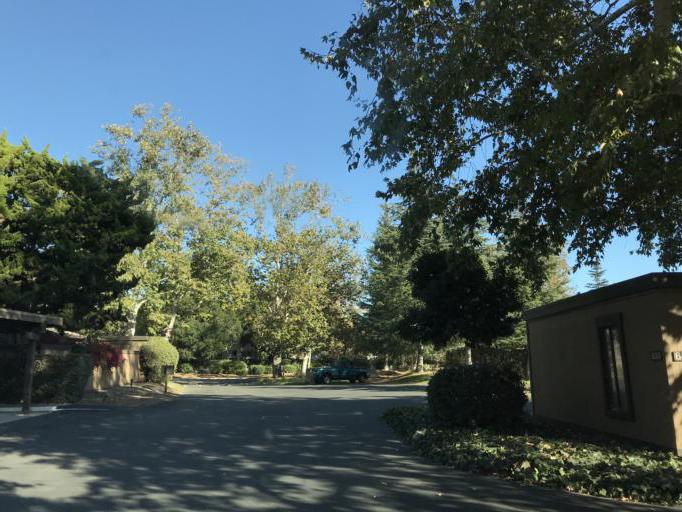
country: US
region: California
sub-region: Santa Barbara County
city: Goleta
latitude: 34.4514
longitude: -119.8124
